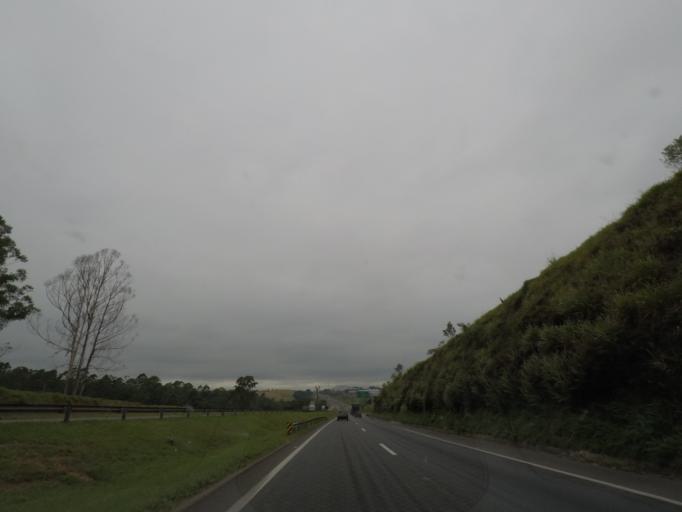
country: BR
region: Sao Paulo
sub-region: Jarinu
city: Jarinu
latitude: -23.0361
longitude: -46.7120
